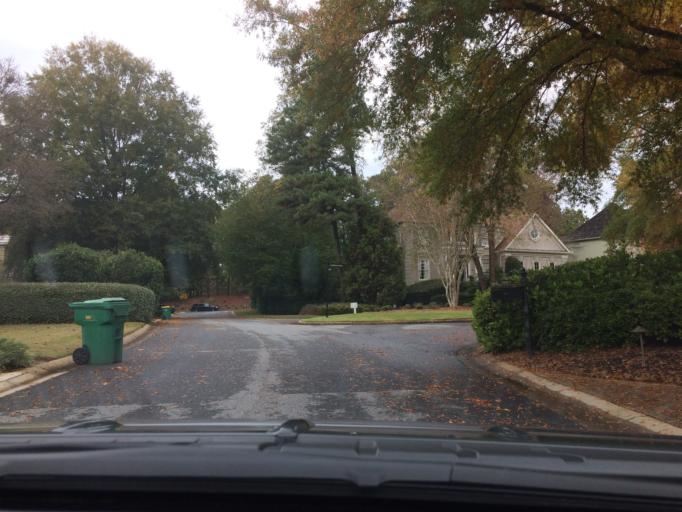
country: US
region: Georgia
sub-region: Fulton County
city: Johns Creek
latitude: 34.0093
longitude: -84.2473
